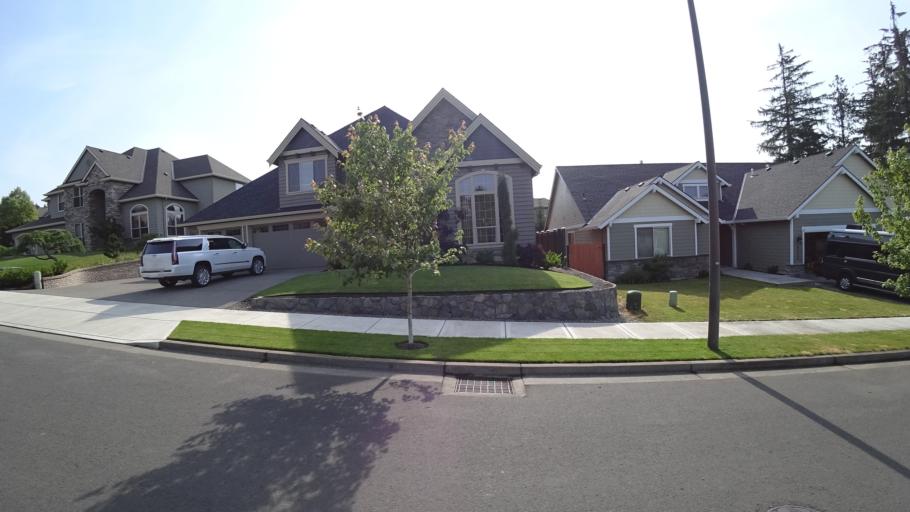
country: US
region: Oregon
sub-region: Clackamas County
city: Happy Valley
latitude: 45.4544
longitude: -122.5198
